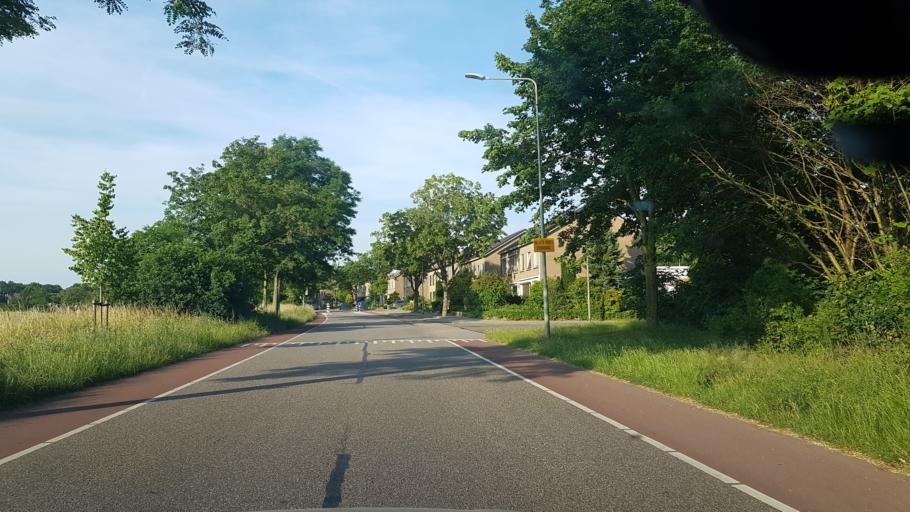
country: NL
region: North Brabant
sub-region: Gemeente Cuijk
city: Cuijk
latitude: 51.7694
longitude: 5.8716
